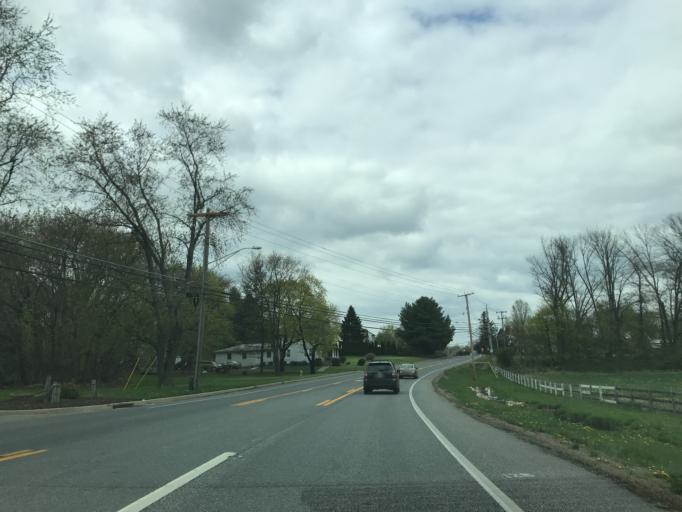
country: US
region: Maryland
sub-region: Harford County
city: Bel Air South
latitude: 39.5318
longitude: -76.2962
